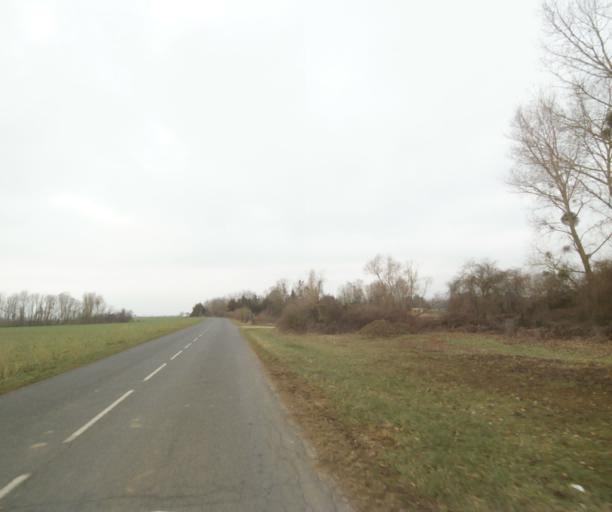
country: FR
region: Champagne-Ardenne
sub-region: Departement de la Haute-Marne
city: Villiers-en-Lieu
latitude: 48.6541
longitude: 4.7869
